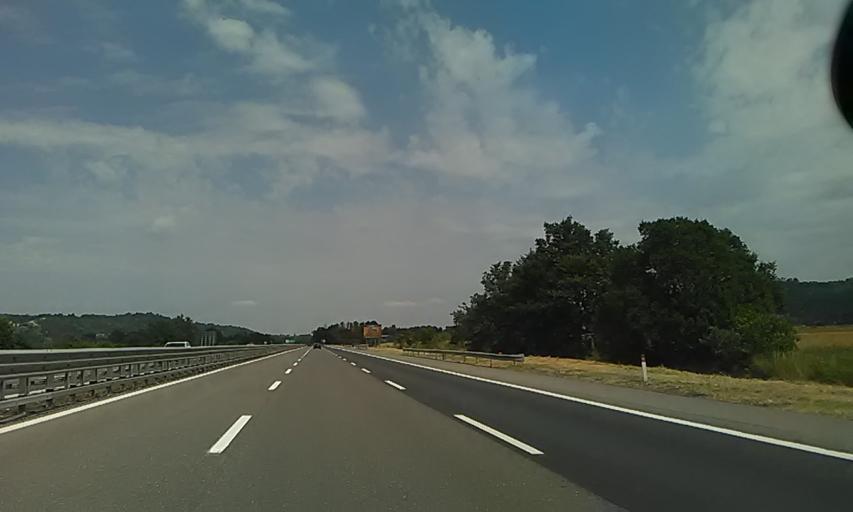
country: IT
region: Piedmont
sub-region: Provincia di Alessandria
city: Rocca Grimalda
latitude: 44.6632
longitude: 8.6592
